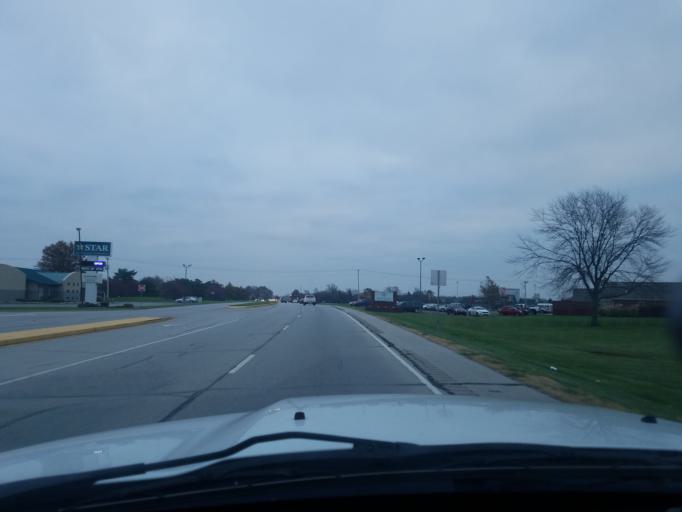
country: US
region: Indiana
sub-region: Delaware County
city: Muncie
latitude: 40.2190
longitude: -85.4265
